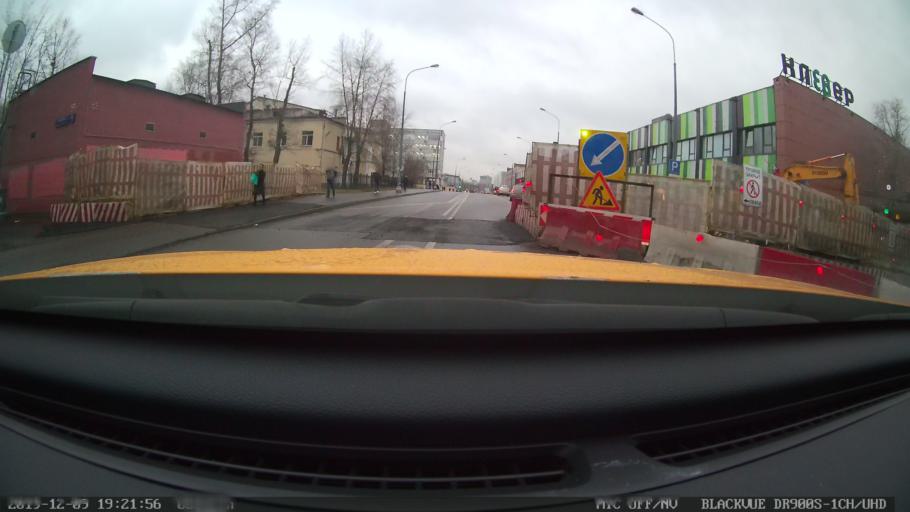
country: RU
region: Moscow
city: Ryazanskiy
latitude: 55.7551
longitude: 37.7525
